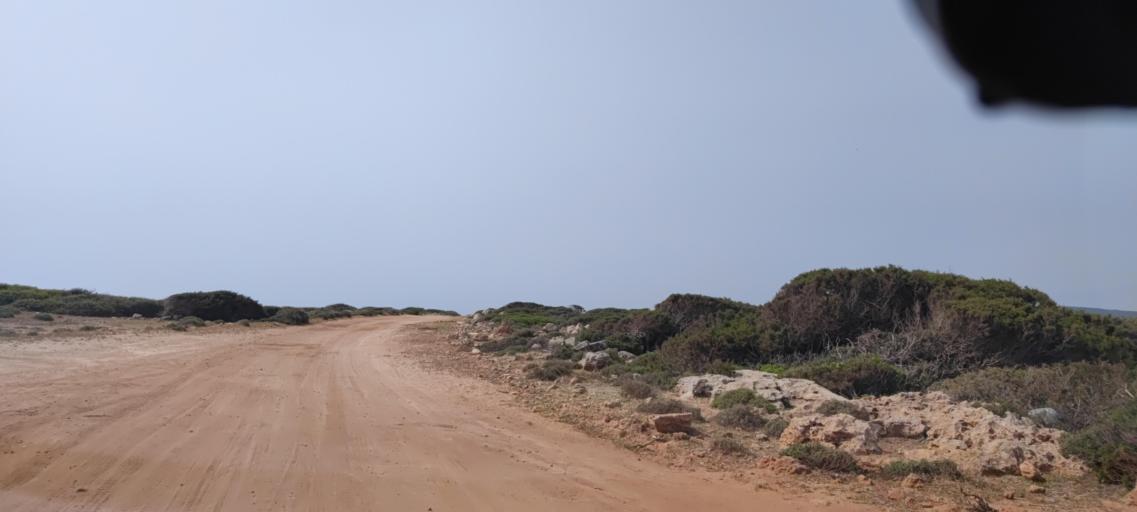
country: CY
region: Ammochostos
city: Rizokarpaso
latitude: 35.6748
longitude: 34.5776
